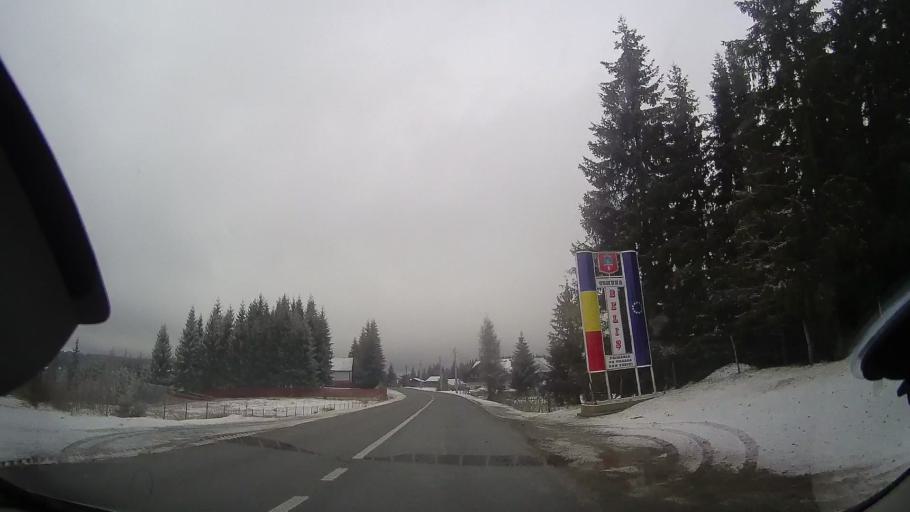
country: RO
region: Cluj
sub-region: Comuna Belis
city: Belis
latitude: 46.6796
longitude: 23.0416
